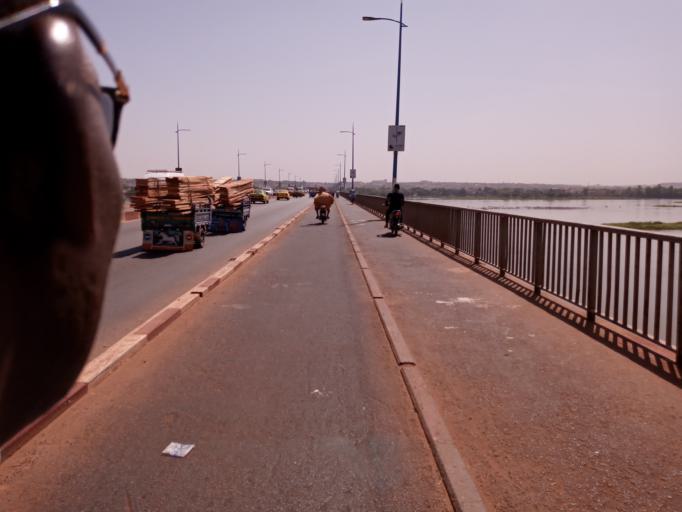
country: ML
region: Bamako
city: Bamako
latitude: 12.6266
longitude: -8.0071
